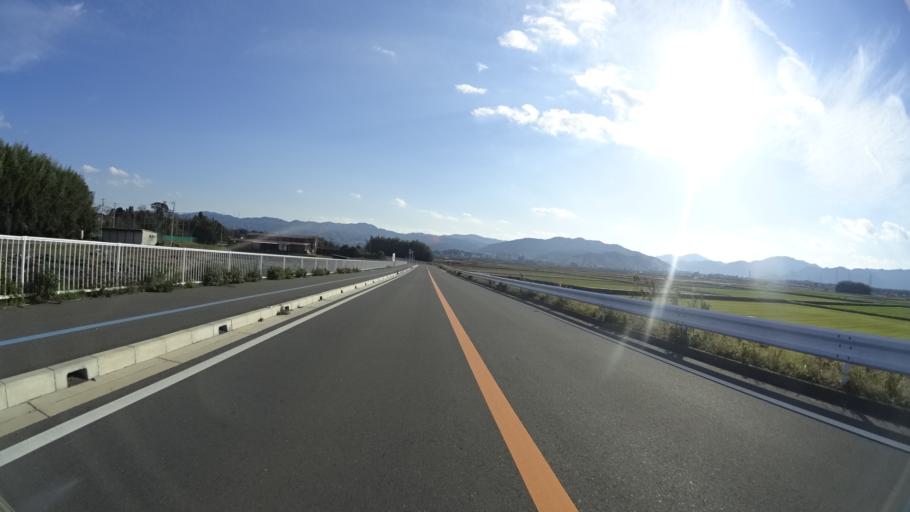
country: JP
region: Kyoto
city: Kameoka
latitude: 35.0350
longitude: 135.5826
